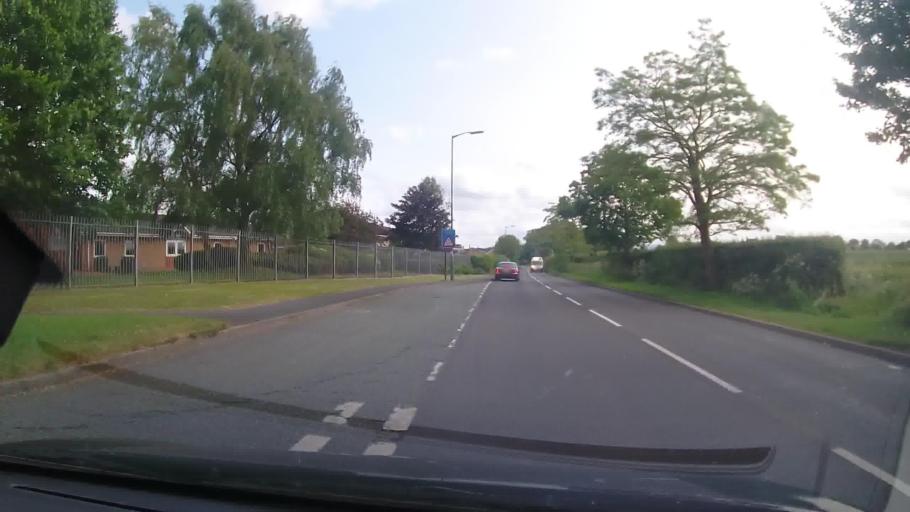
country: GB
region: England
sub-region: Shropshire
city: Shrewsbury
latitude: 52.7376
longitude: -2.7457
